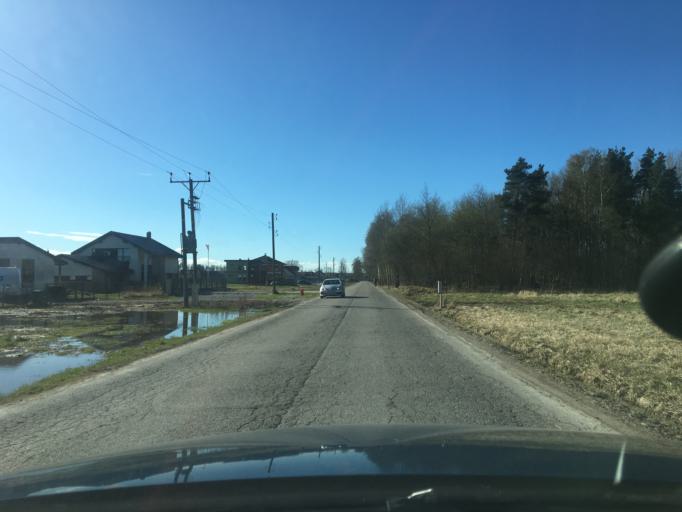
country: LV
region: Salaspils
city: Salaspils
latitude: 56.8736
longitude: 24.3367
